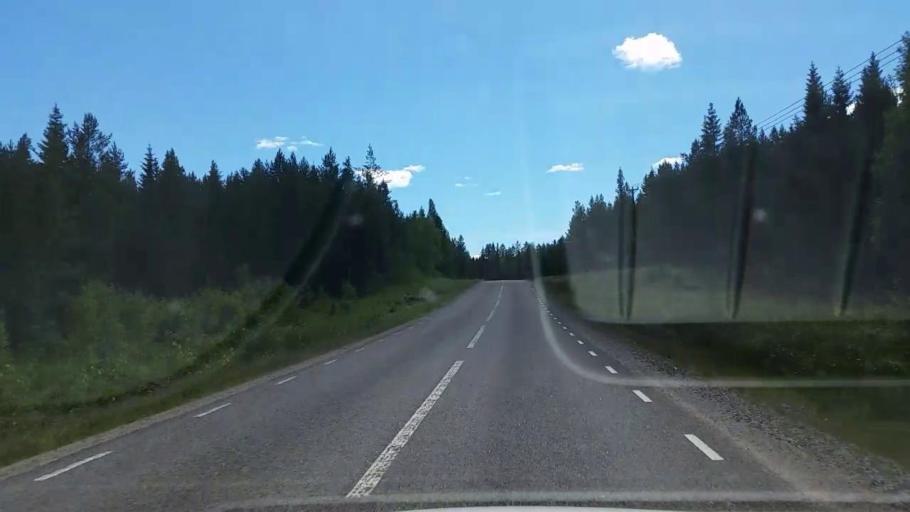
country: SE
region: Gaevleborg
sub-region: Ovanakers Kommun
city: Edsbyn
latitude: 61.5329
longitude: 15.6793
